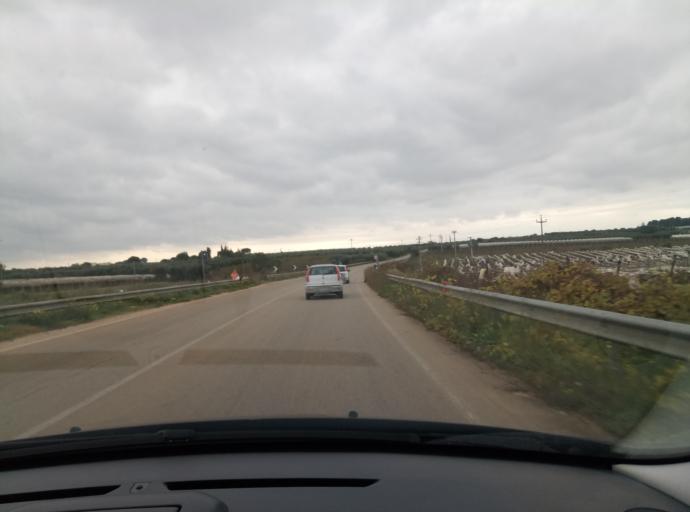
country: IT
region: Apulia
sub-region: Provincia di Bari
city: Adelfia
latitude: 40.9576
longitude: 16.8658
